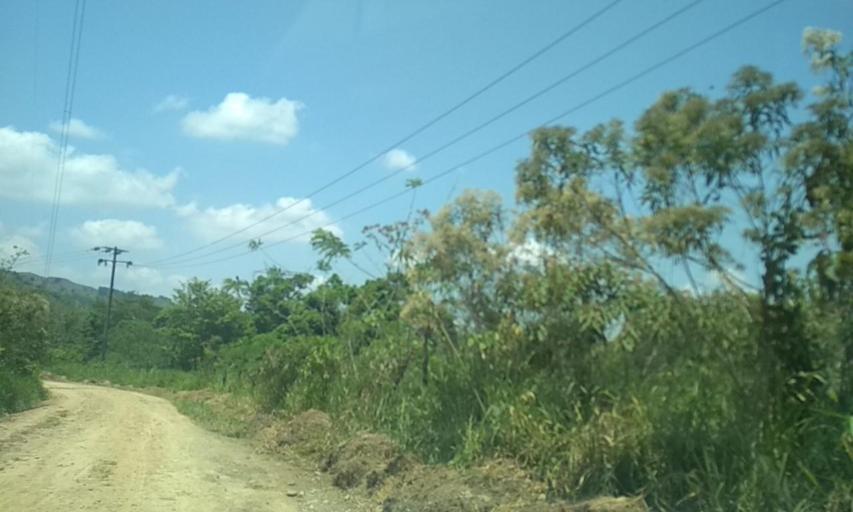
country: MX
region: Chiapas
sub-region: Tecpatan
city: Raudales Malpaso
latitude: 17.3939
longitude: -93.7281
